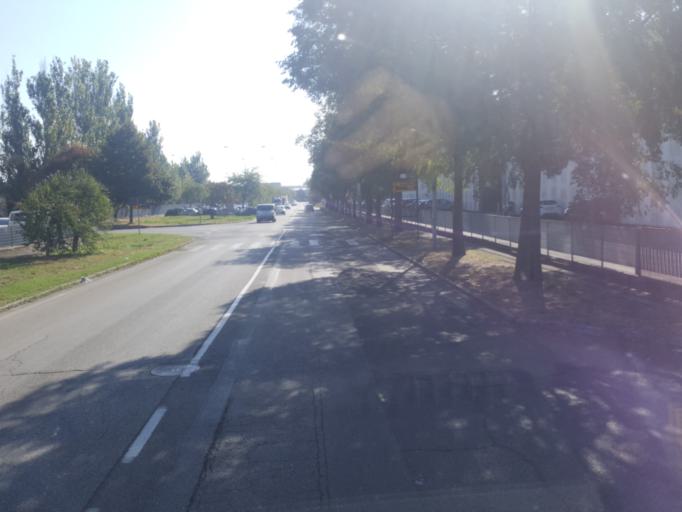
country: IT
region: Emilia-Romagna
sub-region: Provincia di Modena
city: Villanova
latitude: 44.6712
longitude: 10.9324
